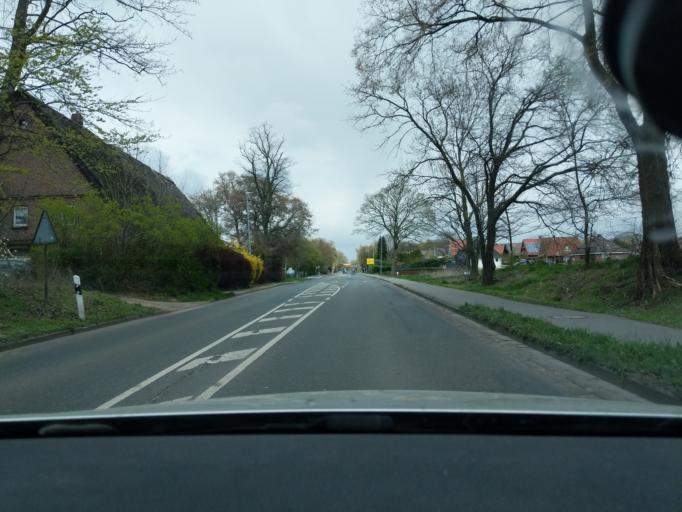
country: DE
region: Lower Saxony
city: Stade
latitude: 53.5800
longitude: 9.4718
